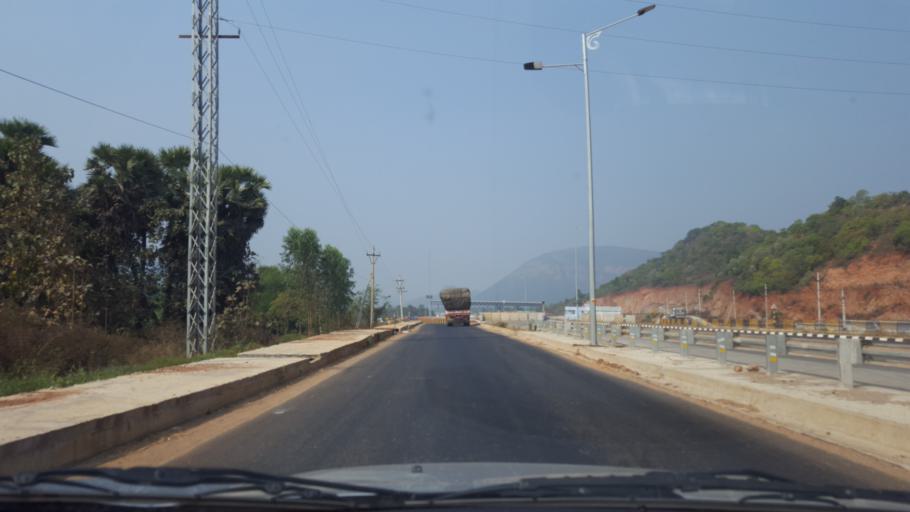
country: IN
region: Andhra Pradesh
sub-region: Vishakhapatnam
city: Bhimunipatnam
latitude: 17.8881
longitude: 83.3488
